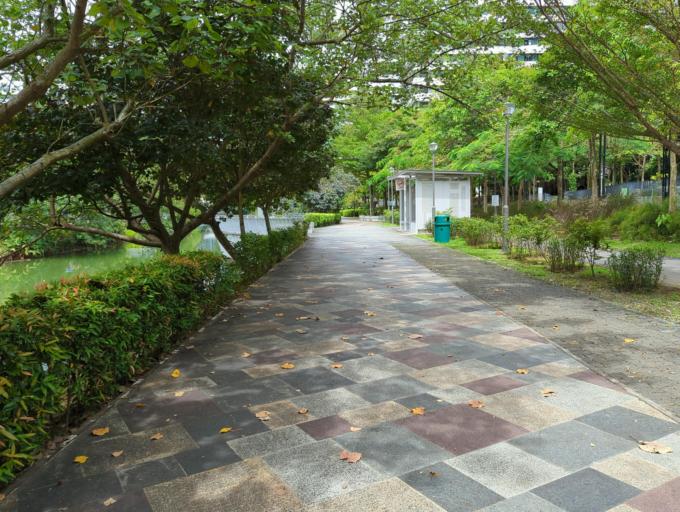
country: MY
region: Johor
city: Kampung Pasir Gudang Baru
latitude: 1.4083
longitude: 103.9013
